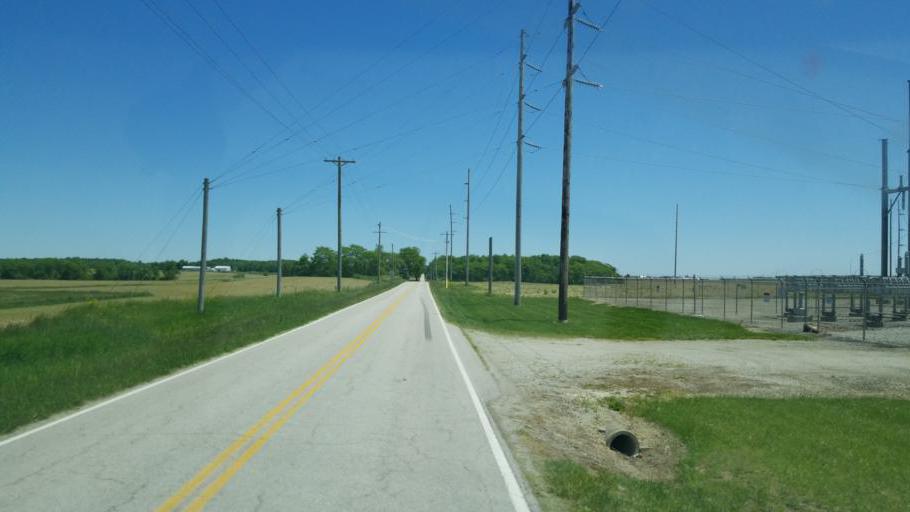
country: US
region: Ohio
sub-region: Darke County
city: Ansonia
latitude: 40.2647
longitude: -84.6359
